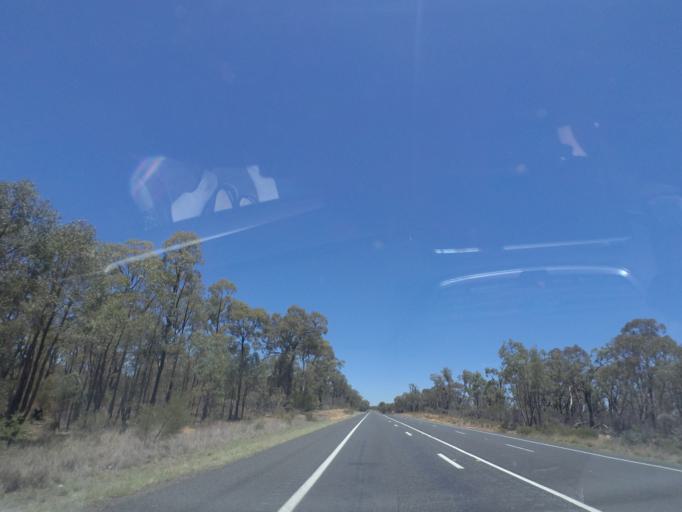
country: AU
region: New South Wales
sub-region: Warrumbungle Shire
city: Coonabarabran
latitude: -30.8760
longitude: 149.4482
